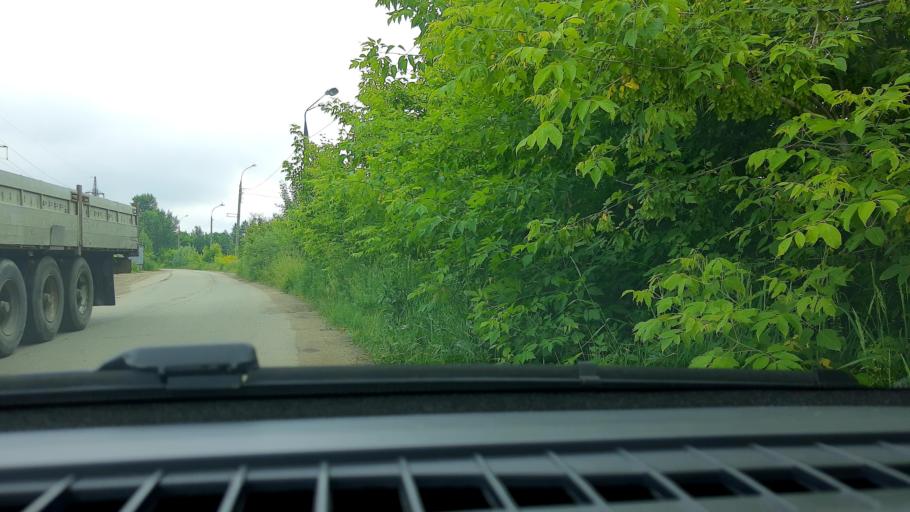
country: RU
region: Nizjnij Novgorod
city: Burevestnik
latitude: 56.2284
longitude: 43.8857
